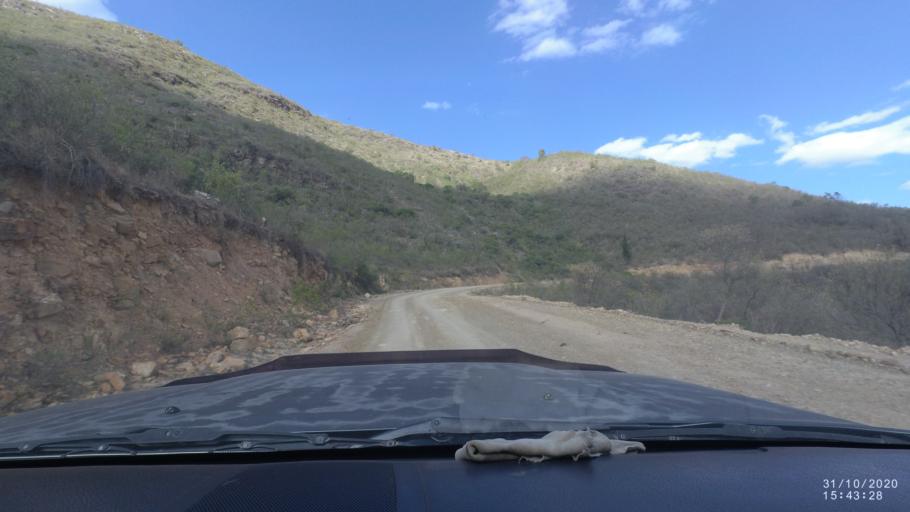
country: BO
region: Chuquisaca
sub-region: Provincia Zudanez
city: Mojocoya
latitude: -18.3183
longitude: -64.7281
